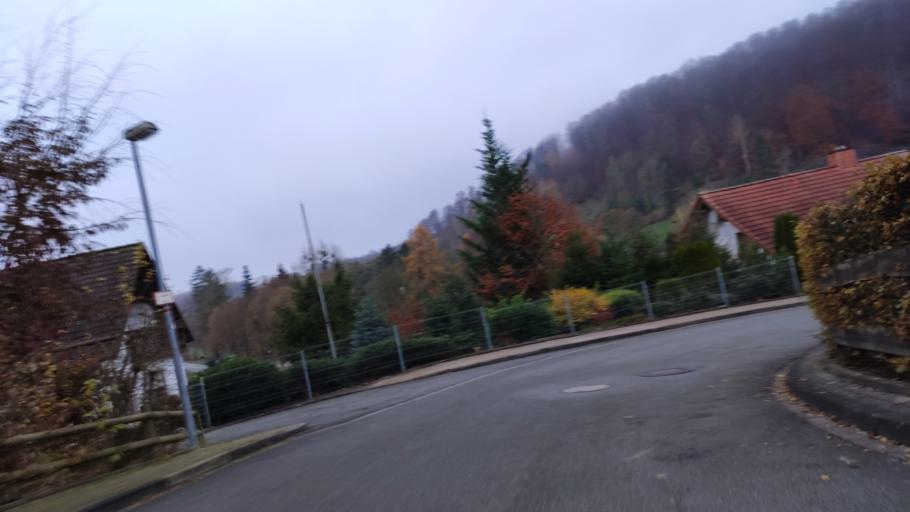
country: DE
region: North Rhine-Westphalia
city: Beverungen
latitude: 51.7005
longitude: 9.2824
